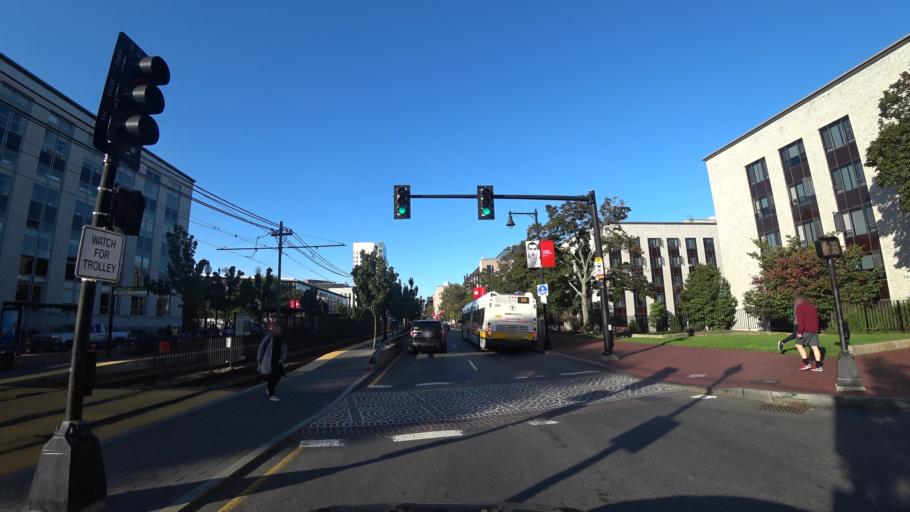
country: US
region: Massachusetts
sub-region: Norfolk County
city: Brookline
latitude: 42.3405
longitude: -71.0887
